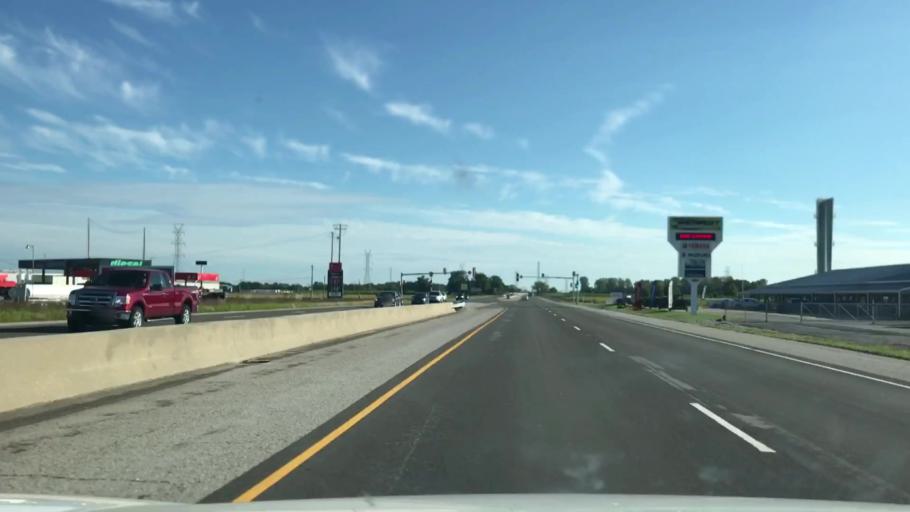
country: US
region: Illinois
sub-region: Madison County
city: Hartford
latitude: 38.8153
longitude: -90.0986
